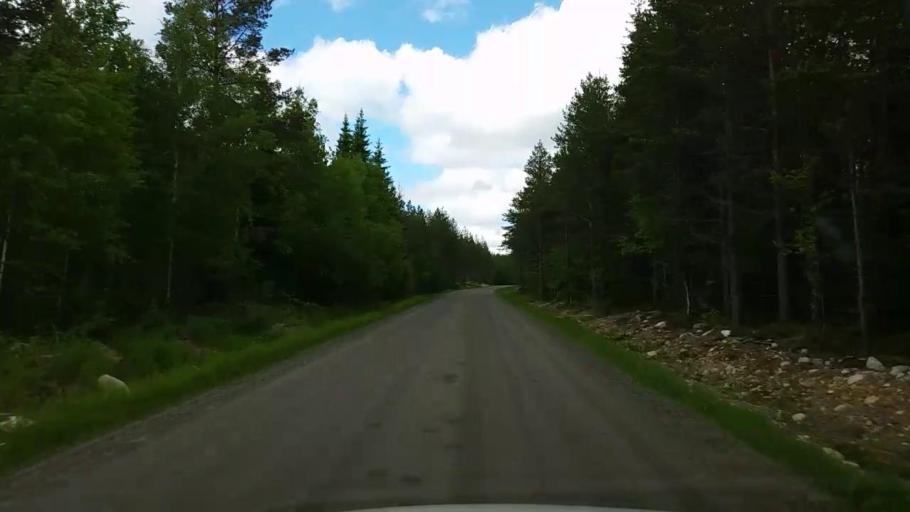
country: SE
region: Gaevleborg
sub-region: Bollnas Kommun
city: Vittsjo
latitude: 61.1575
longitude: 16.1593
